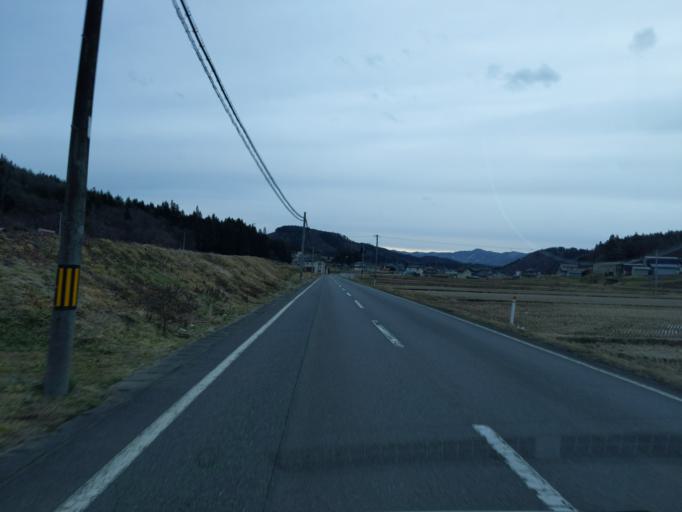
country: JP
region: Iwate
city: Mizusawa
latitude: 39.0481
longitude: 141.2936
